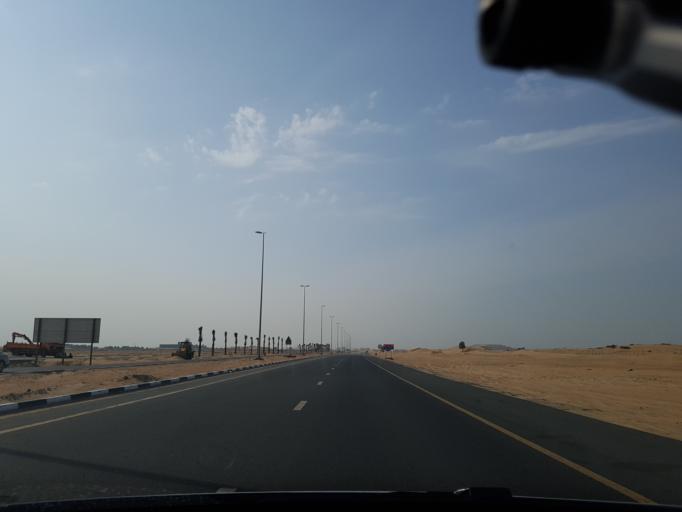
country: AE
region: Ajman
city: Ajman
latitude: 25.4055
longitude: 55.5773
